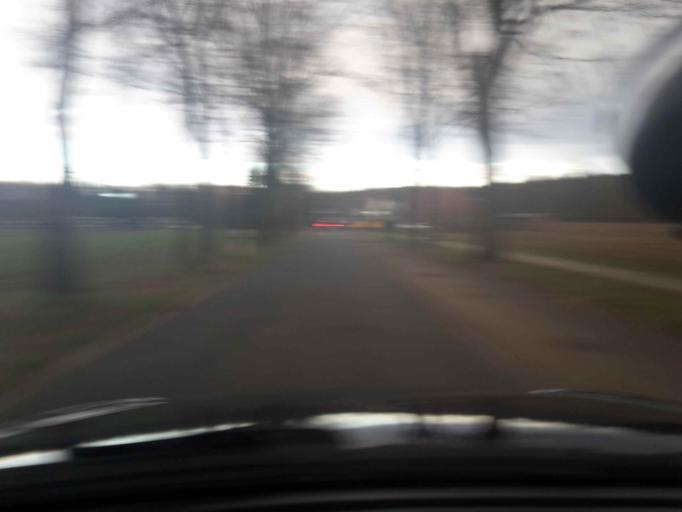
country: DE
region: Lower Saxony
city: Buchholz in der Nordheide
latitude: 53.2837
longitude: 9.9084
